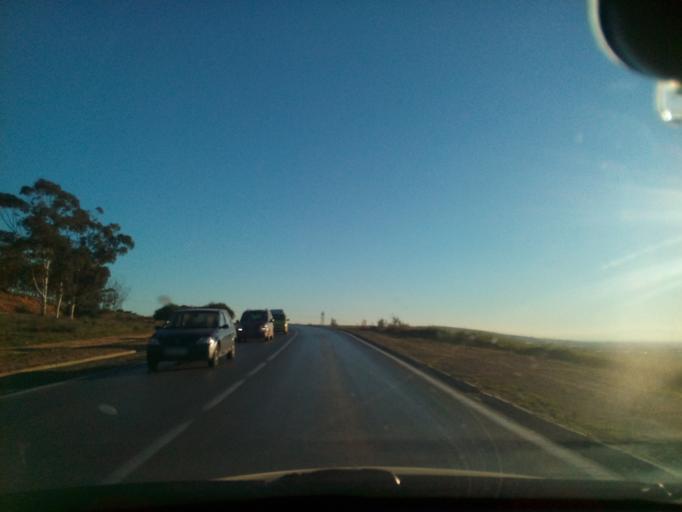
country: DZ
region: Mostaganem
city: Mostaganem
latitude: 35.7663
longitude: 0.2002
